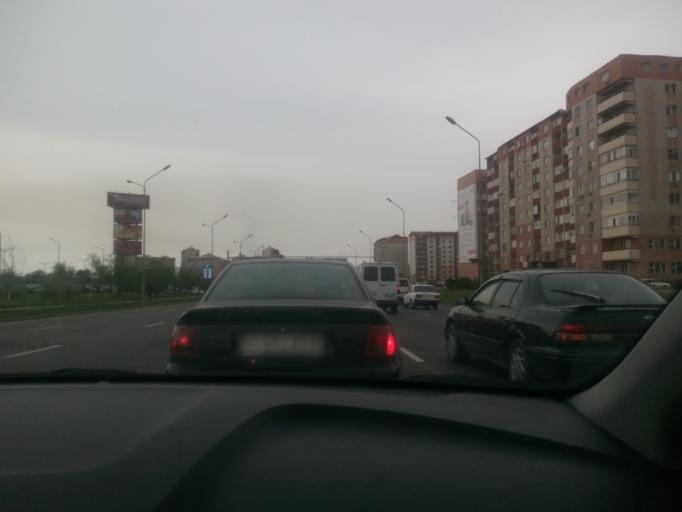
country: KZ
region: Almaty Qalasy
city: Almaty
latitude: 43.2493
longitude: 76.8252
